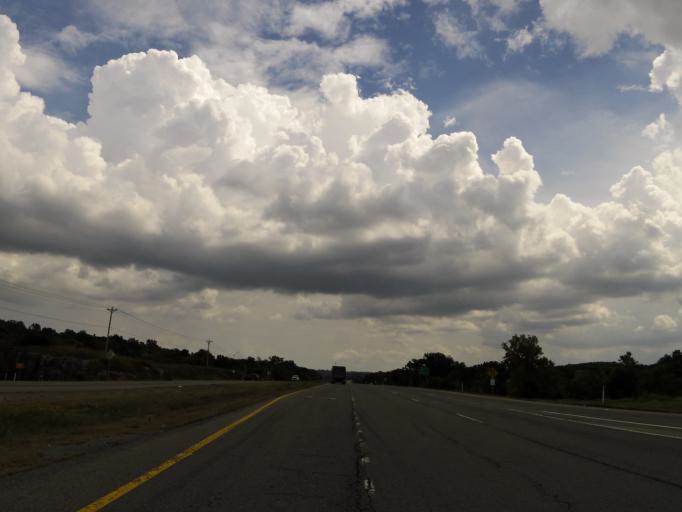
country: US
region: Tennessee
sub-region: Wilson County
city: Rural Hill
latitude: 36.1839
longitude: -86.4067
